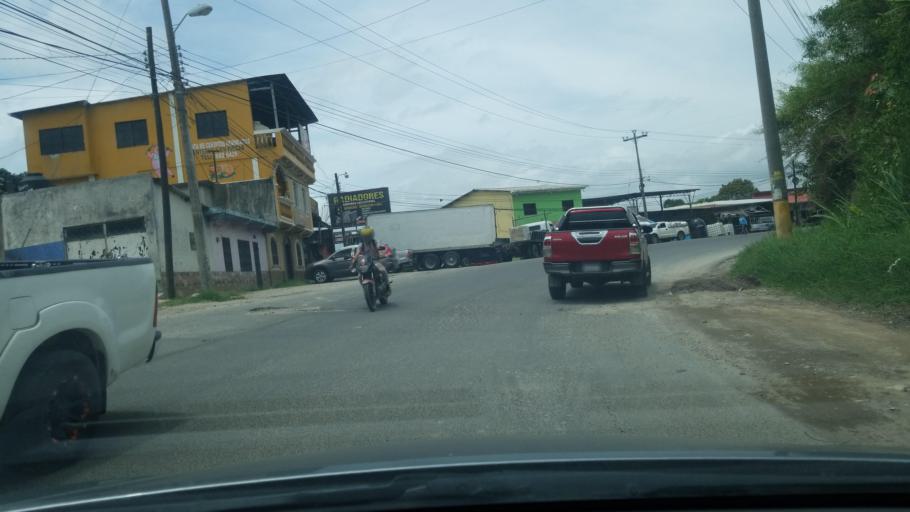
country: HN
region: Copan
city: Santa Rosa de Copan
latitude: 14.7554
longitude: -88.7757
